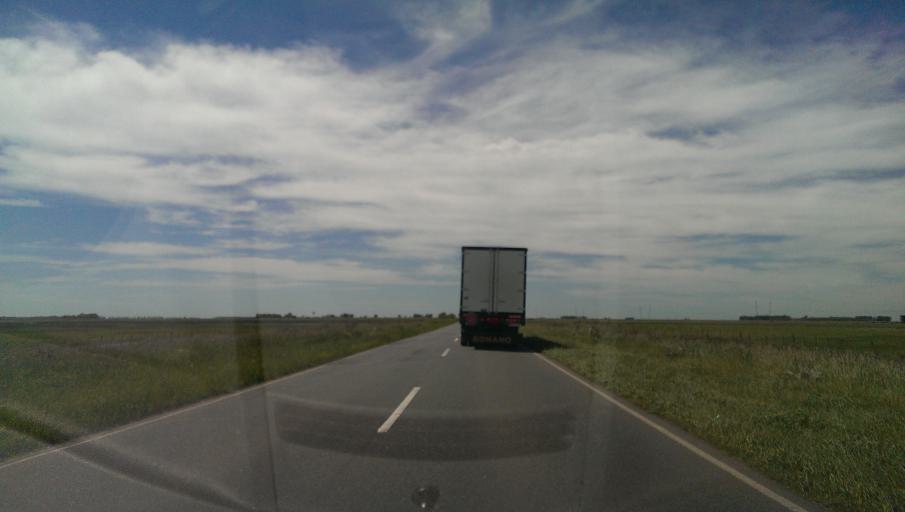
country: AR
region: Buenos Aires
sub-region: Partido de Laprida
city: Laprida
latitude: -37.3531
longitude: -60.9416
